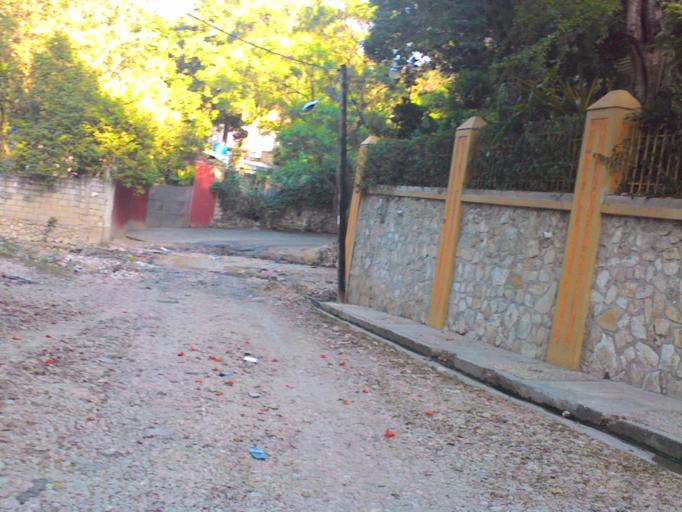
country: HT
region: Ouest
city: Delmas 73
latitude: 18.5309
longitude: -72.3047
